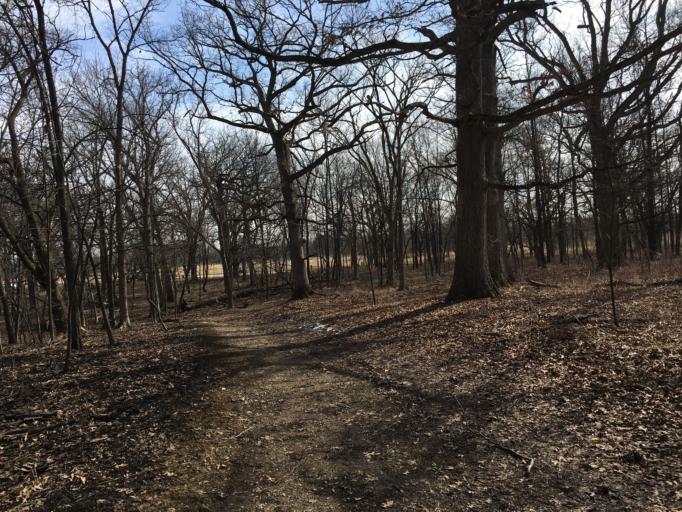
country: US
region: Illinois
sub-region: Cook County
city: Streamwood
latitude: 42.0511
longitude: -88.1983
